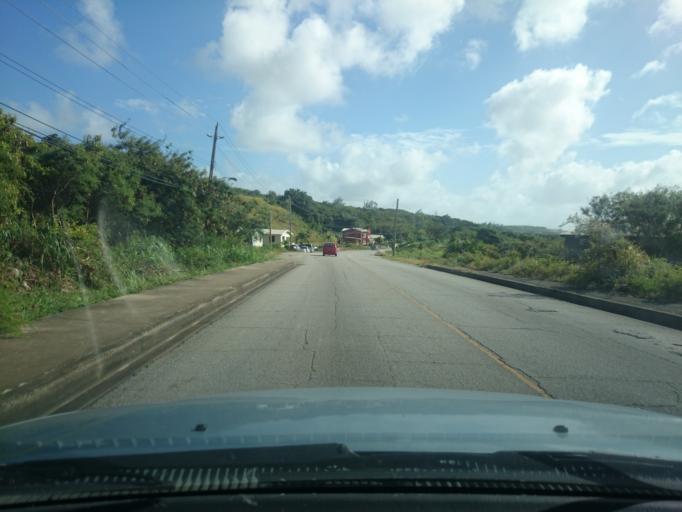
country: BB
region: Saint Lucy
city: Checker Hall
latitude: 13.2830
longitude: -59.6208
